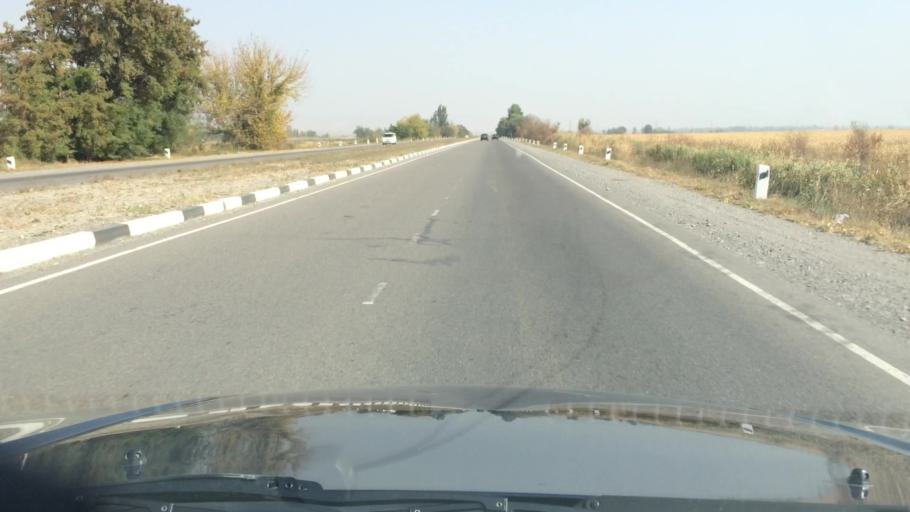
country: KG
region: Chuy
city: Kant
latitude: 42.9563
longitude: 74.7955
